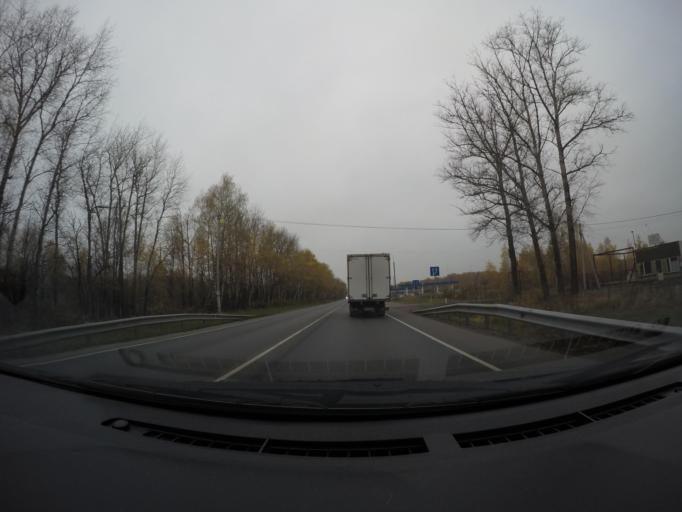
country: RU
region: Moskovskaya
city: Bronnitsy
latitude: 55.3790
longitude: 38.1790
